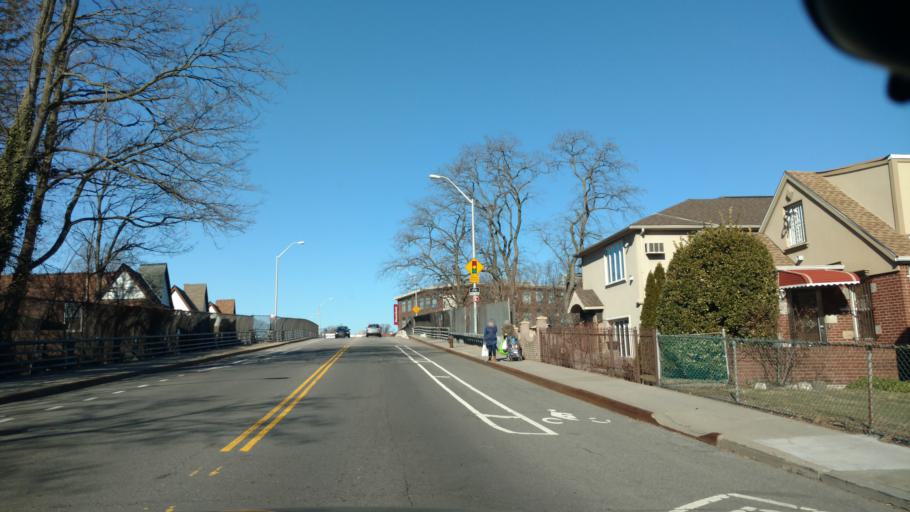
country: US
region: New York
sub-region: Queens County
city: Borough of Queens
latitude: 40.7061
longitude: -73.8688
